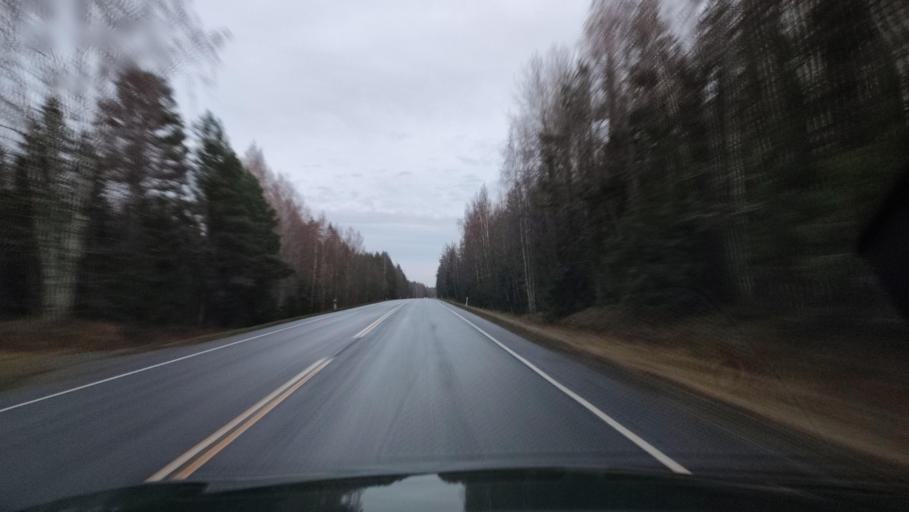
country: FI
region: Ostrobothnia
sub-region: Vaasa
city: Ristinummi
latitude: 63.0158
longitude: 21.7598
